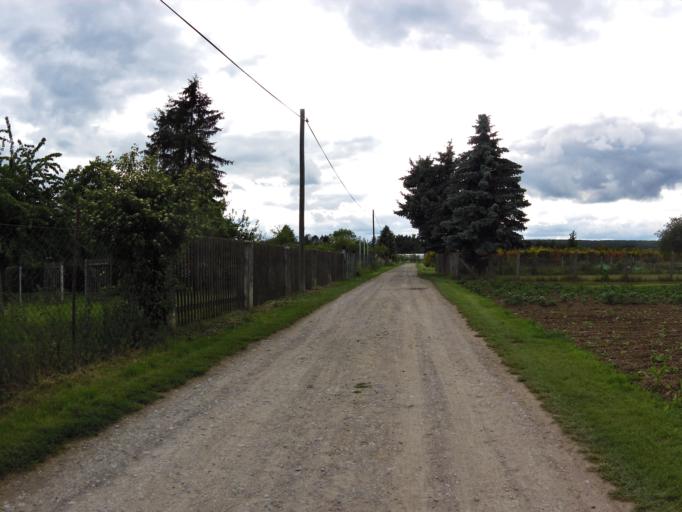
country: DE
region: Thuringia
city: Langula
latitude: 51.1532
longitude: 10.4175
